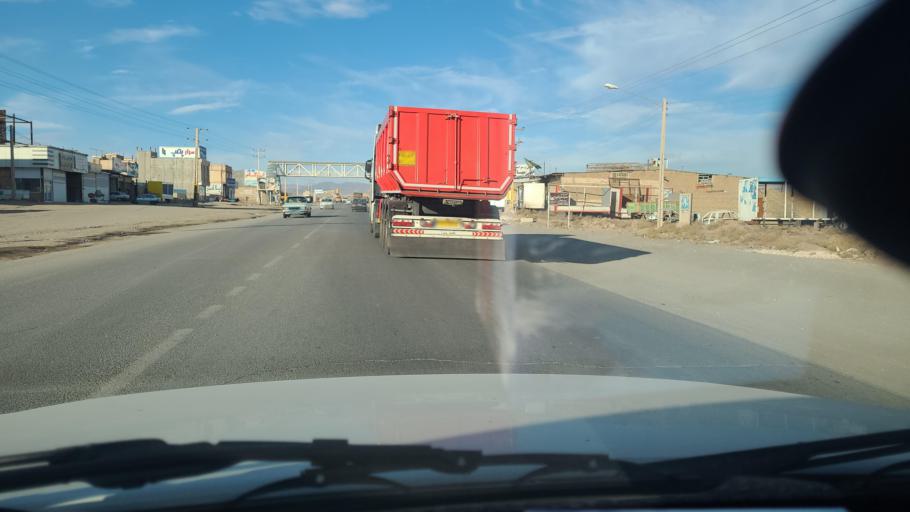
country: IR
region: Razavi Khorasan
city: Sabzevar
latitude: 36.2204
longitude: 57.6515
